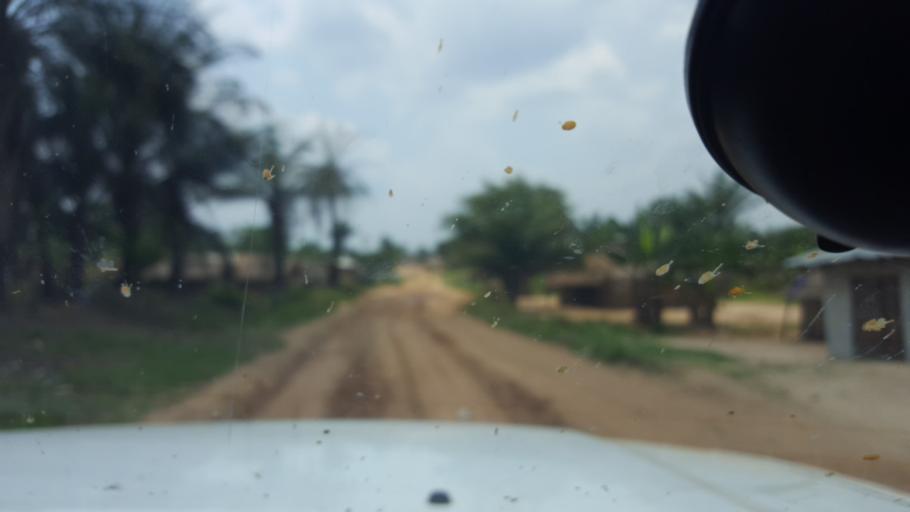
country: CD
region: Bandundu
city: Mushie
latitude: -3.7451
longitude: 16.6509
